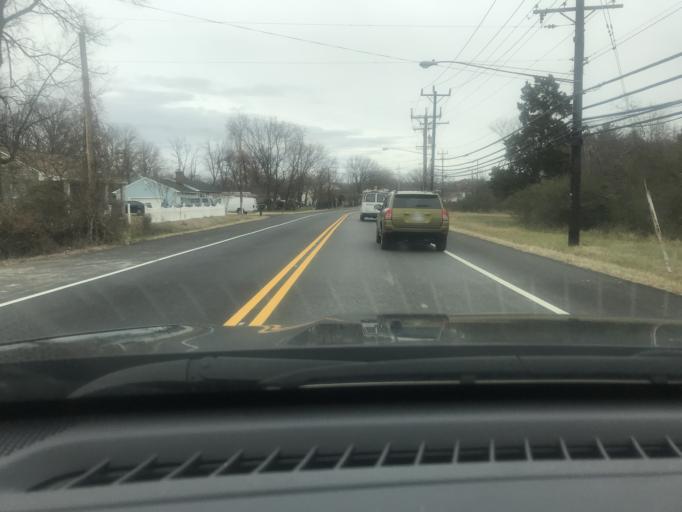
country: US
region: Maryland
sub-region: Prince George's County
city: Friendly
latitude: 38.7743
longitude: -76.9600
